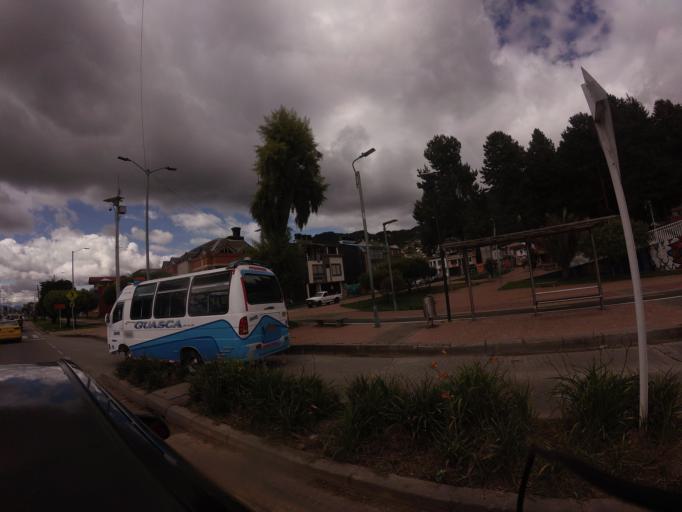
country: CO
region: Cundinamarca
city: Sopo
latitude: 4.9081
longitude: -73.9432
